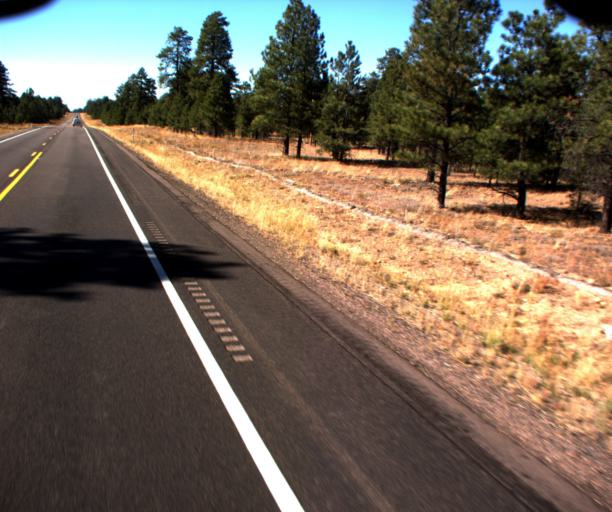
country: US
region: Arizona
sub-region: Apache County
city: Saint Michaels
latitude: 35.6904
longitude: -109.2552
